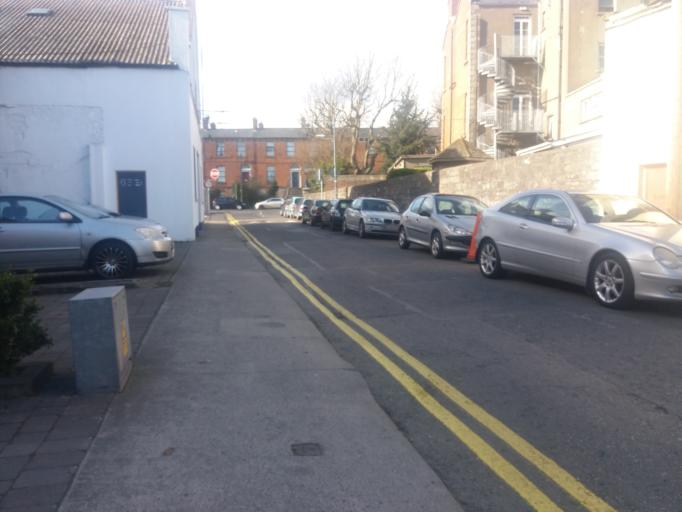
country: IE
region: Leinster
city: Cabra
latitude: 53.3582
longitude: -6.2819
